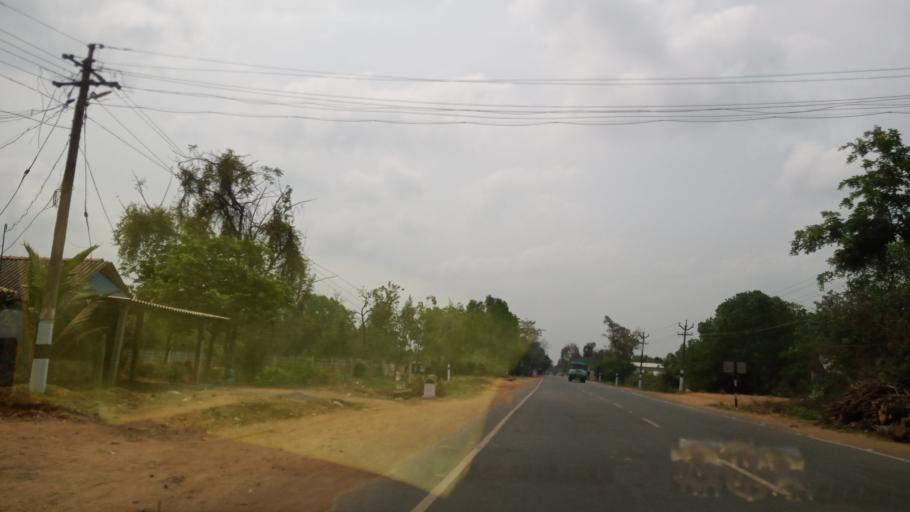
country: IN
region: Tamil Nadu
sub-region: Ariyalur
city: Jayamkondacholapuram
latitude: 11.1553
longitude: 79.3700
